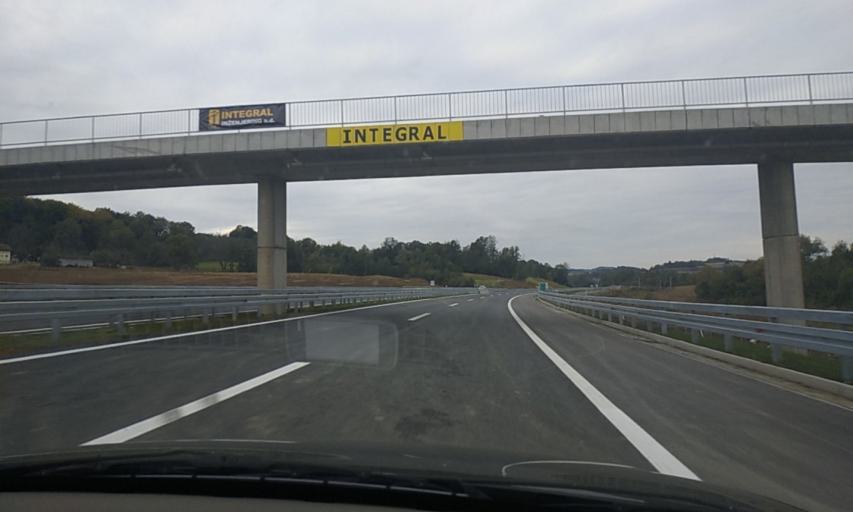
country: BA
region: Republika Srpska
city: Maglajani
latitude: 44.8613
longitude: 17.4842
